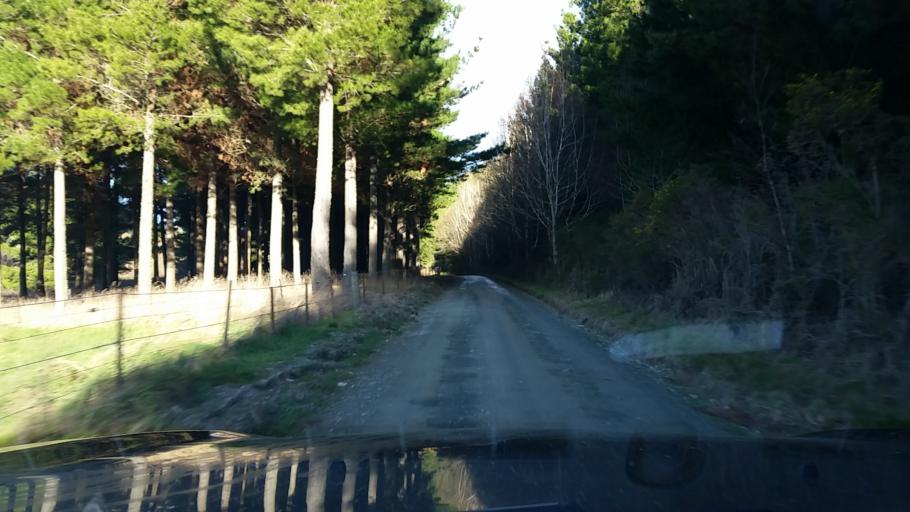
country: NZ
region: Nelson
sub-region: Nelson City
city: Nelson
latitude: -41.5519
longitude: 173.4223
